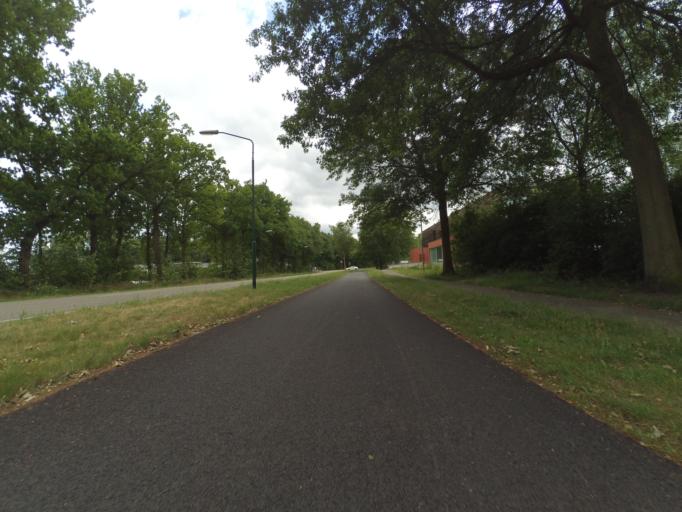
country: NL
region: North Brabant
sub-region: Gemeente Woensdrecht
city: Woensdrecht
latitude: 51.4187
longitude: 4.3359
